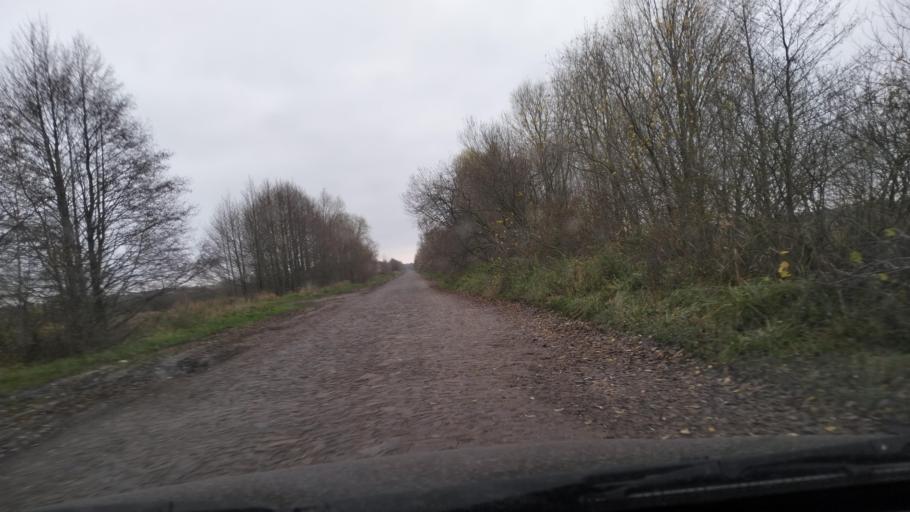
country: BY
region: Brest
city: Davyd-Haradok
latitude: 51.9877
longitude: 27.2054
